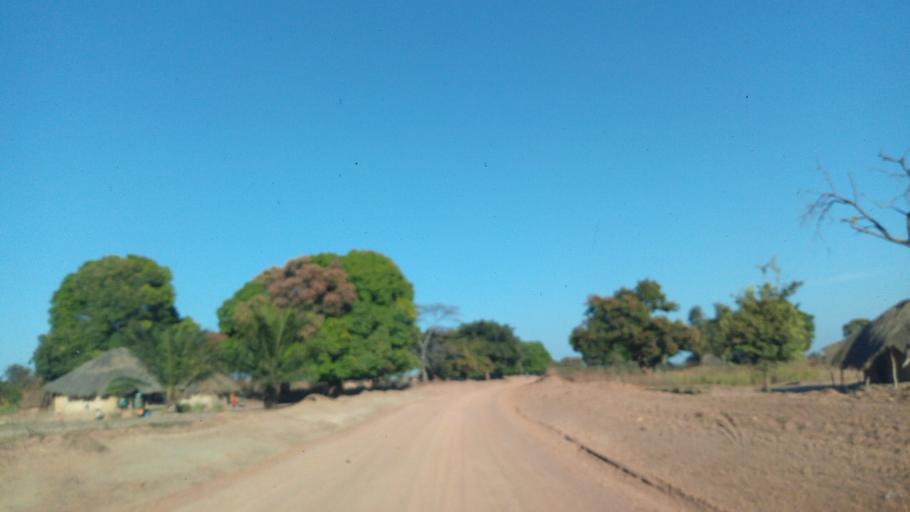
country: ZM
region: Luapula
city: Mwense
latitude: -10.4452
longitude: 28.5760
